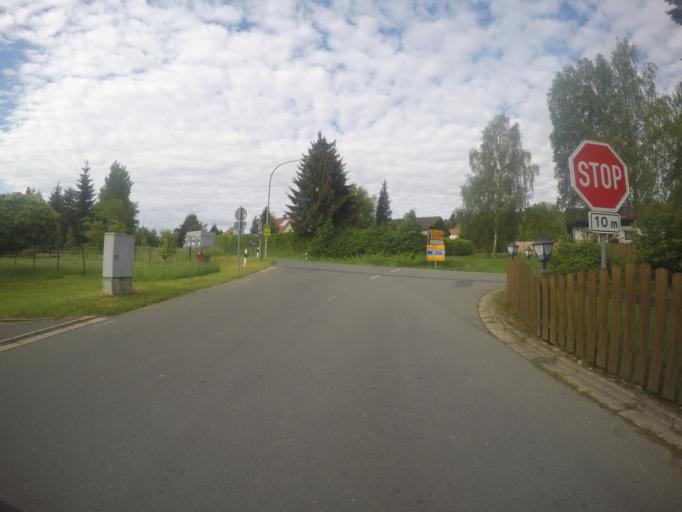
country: DE
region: Bavaria
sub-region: Upper Franconia
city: Schonwald
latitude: 50.2095
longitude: 12.0953
